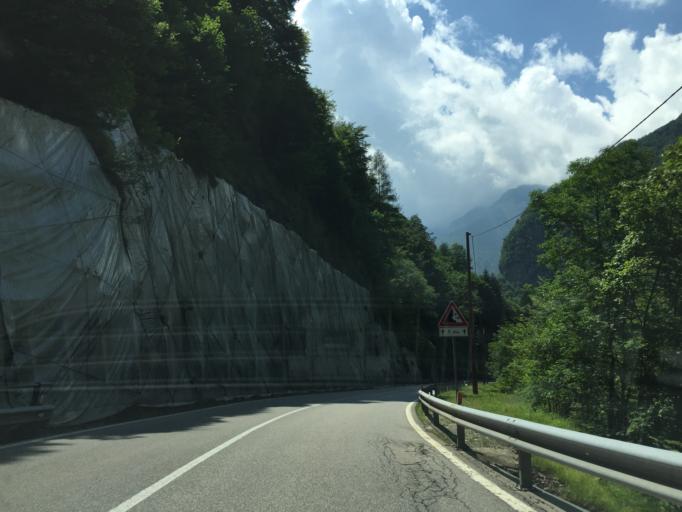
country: IT
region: Trentino-Alto Adige
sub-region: Provincia di Trento
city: Imer
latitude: 46.1084
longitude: 11.7779
